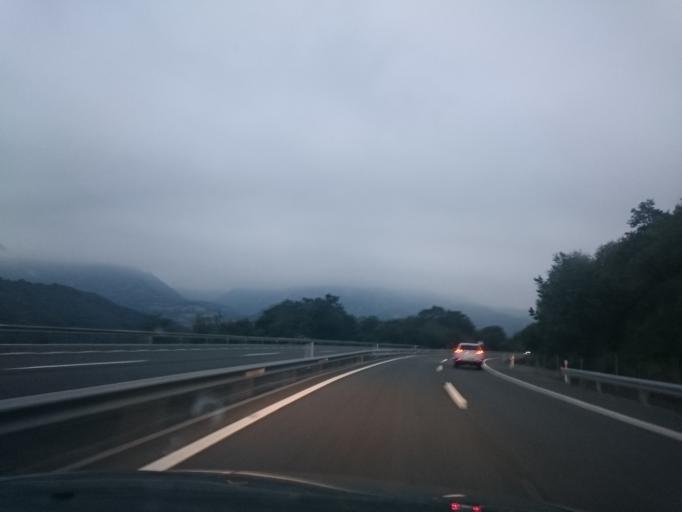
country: ES
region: Asturias
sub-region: Province of Asturias
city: Pola de Lena
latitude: 43.0672
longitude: -5.8253
